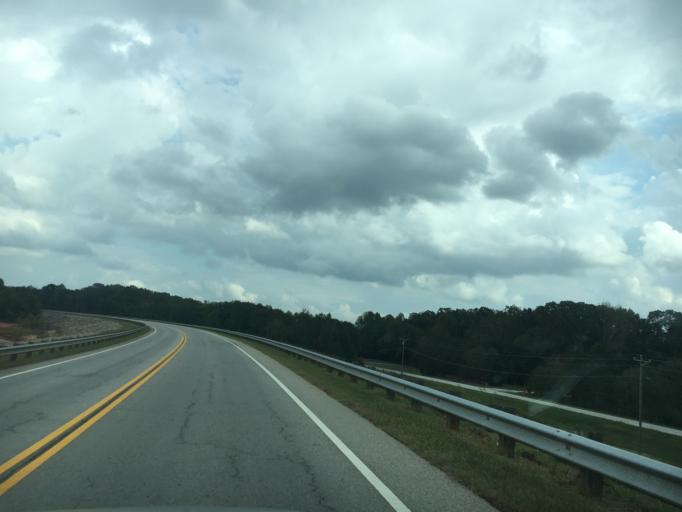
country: US
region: Georgia
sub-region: Hart County
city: Hartwell
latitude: 34.3378
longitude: -82.8430
